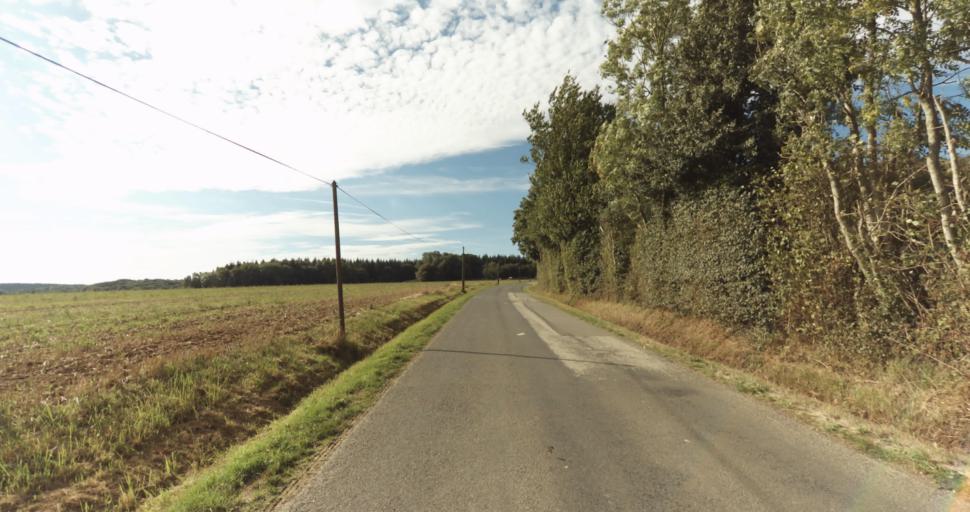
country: FR
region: Lower Normandy
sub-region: Departement de l'Orne
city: Gace
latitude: 48.8287
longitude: 0.2388
